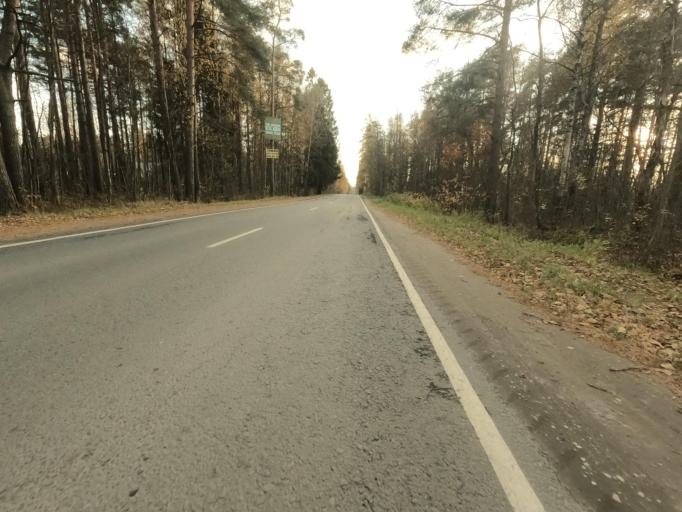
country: RU
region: St.-Petersburg
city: Beloostrov
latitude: 60.1657
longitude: 30.0096
